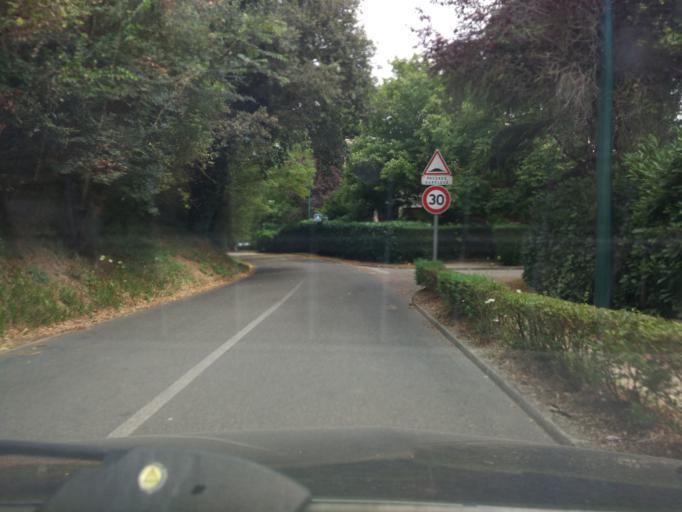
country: FR
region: Ile-de-France
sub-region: Departement de l'Essonne
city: Villiers-le-Bacle
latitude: 48.7074
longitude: 2.1208
